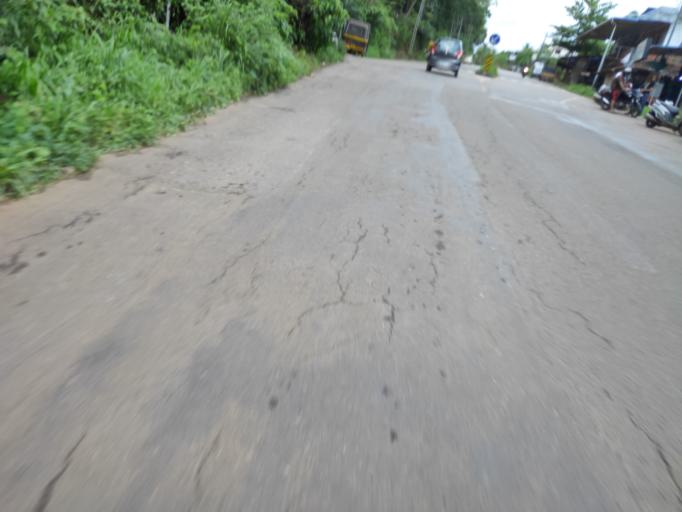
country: IN
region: Kerala
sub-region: Malappuram
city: Manjeri
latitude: 11.1975
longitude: 76.2256
